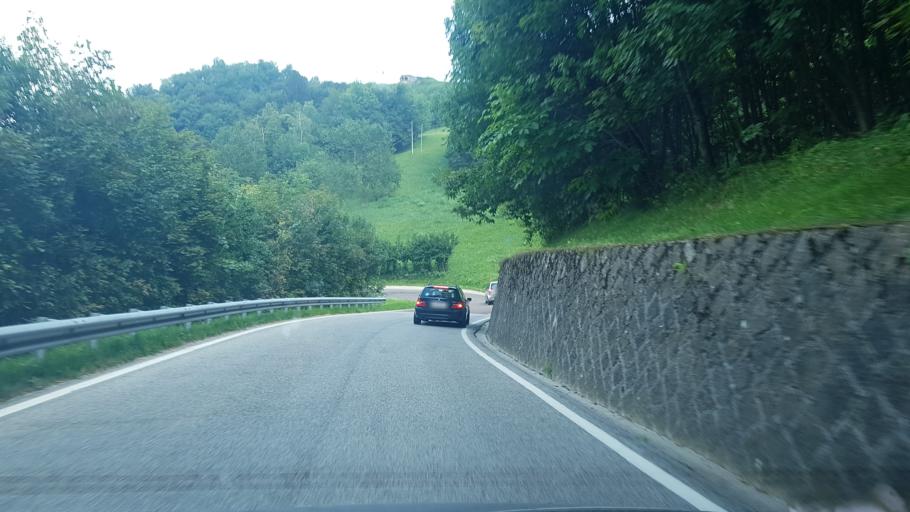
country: IT
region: Veneto
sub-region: Provincia di Vicenza
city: Recoaro Terme
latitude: 45.7586
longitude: 11.2060
